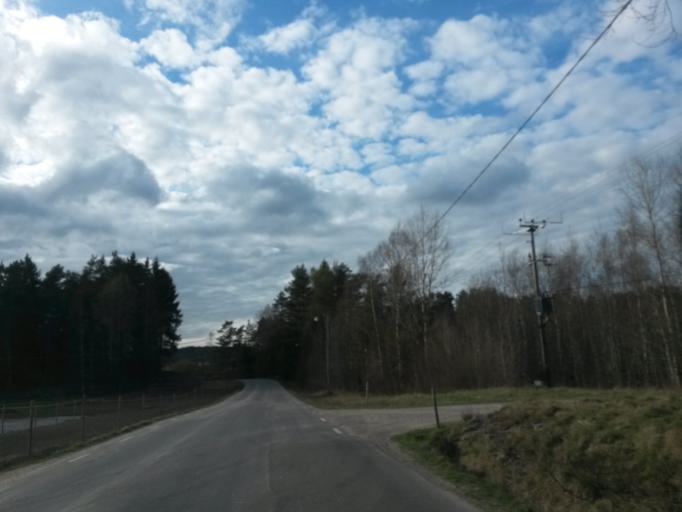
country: SE
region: Vaestra Goetaland
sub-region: Vargarda Kommun
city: Jonstorp
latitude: 58.0160
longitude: 12.6481
